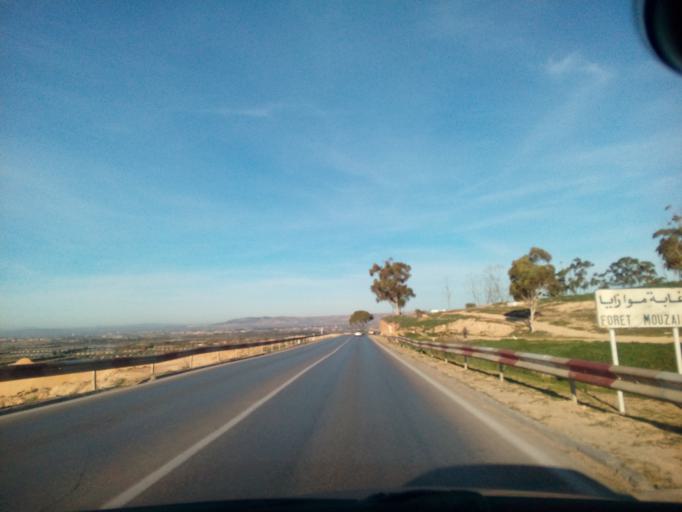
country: DZ
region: Mostaganem
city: Mostaganem
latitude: 35.7639
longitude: 0.2030
